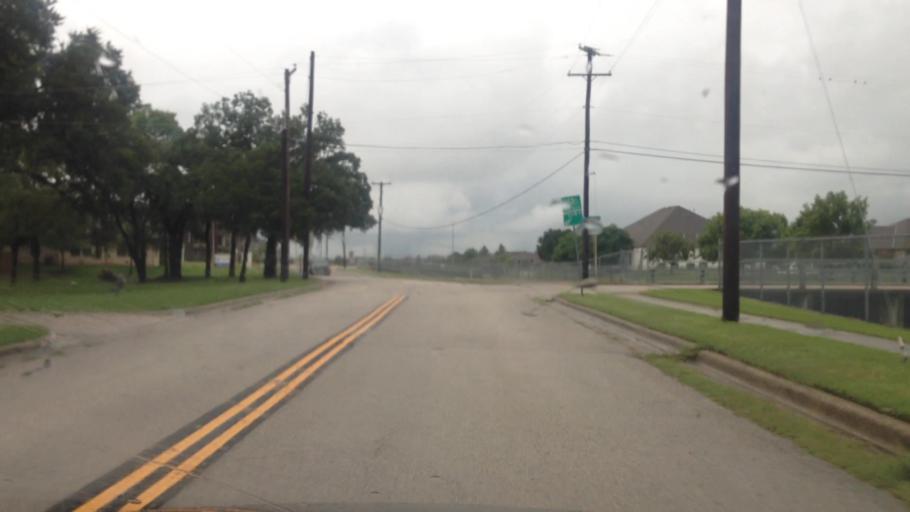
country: US
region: Texas
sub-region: Tarrant County
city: North Richland Hills
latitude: 32.8635
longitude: -97.1996
